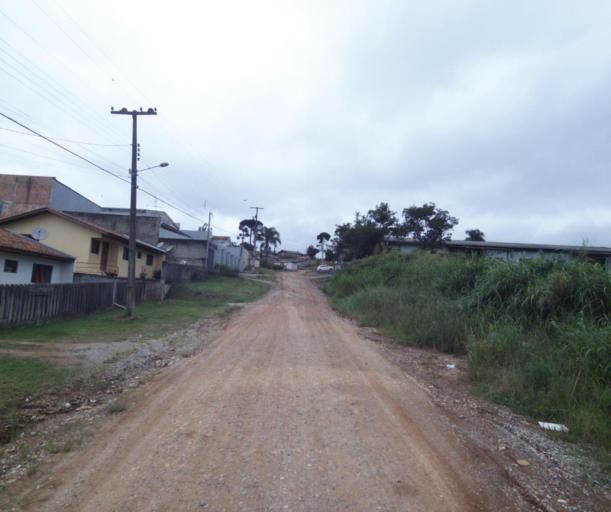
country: BR
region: Parana
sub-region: Quatro Barras
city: Quatro Barras
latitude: -25.3651
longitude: -49.1110
